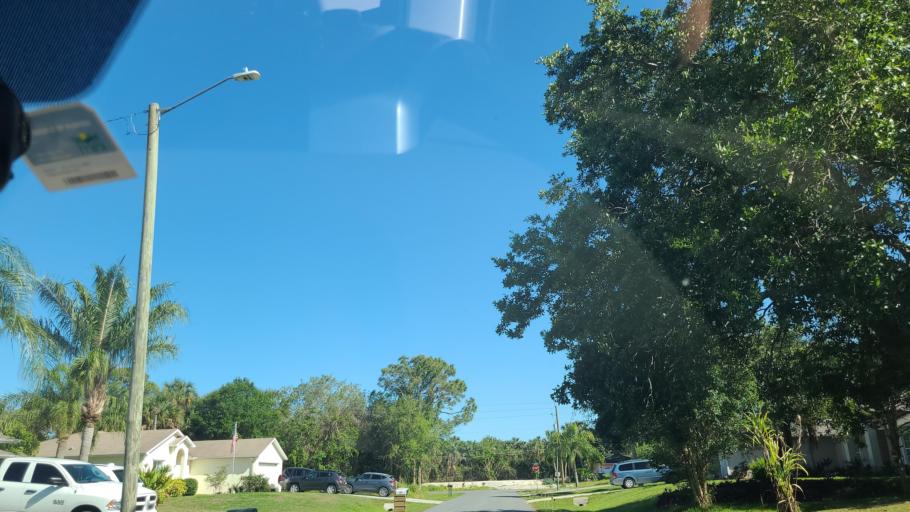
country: US
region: Florida
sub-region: Indian River County
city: Sebastian
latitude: 27.7768
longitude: -80.4831
